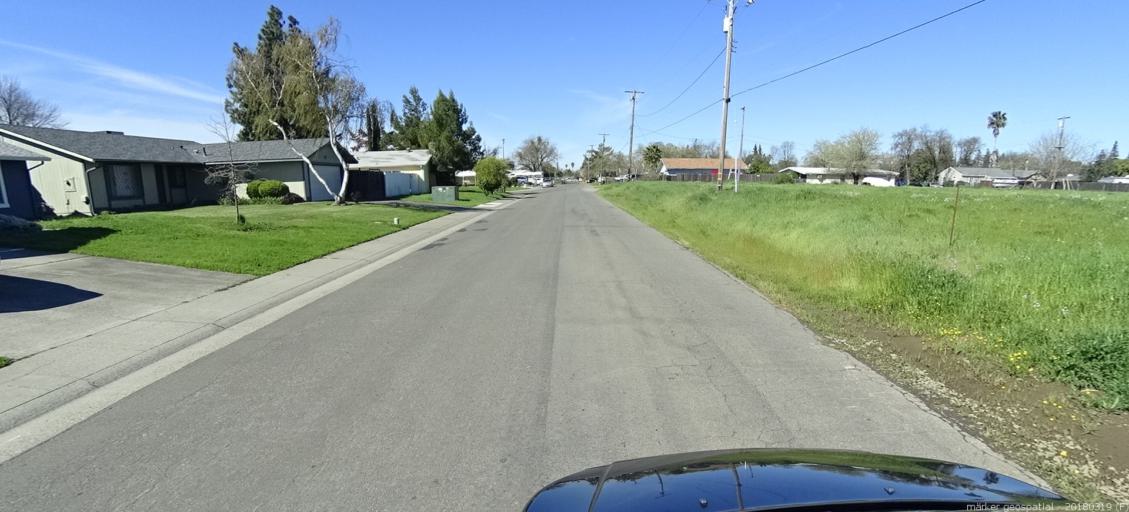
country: US
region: California
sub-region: Sacramento County
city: Parkway
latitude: 38.4843
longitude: -121.4361
